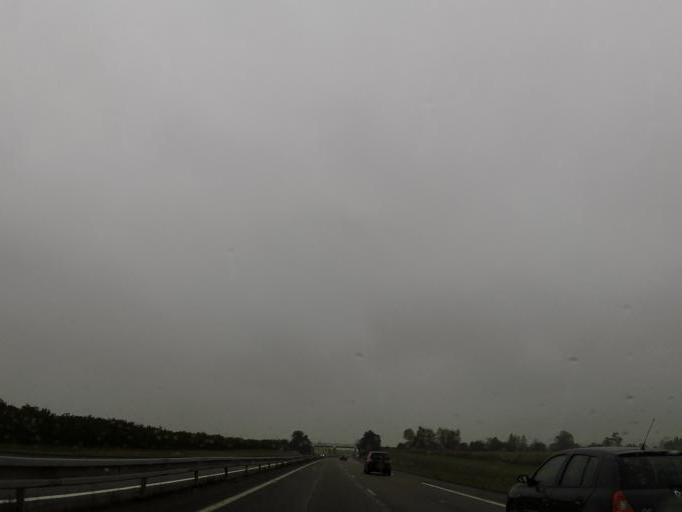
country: FR
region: Champagne-Ardenne
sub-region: Departement de la Marne
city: Suippes
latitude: 49.0522
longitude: 4.6774
